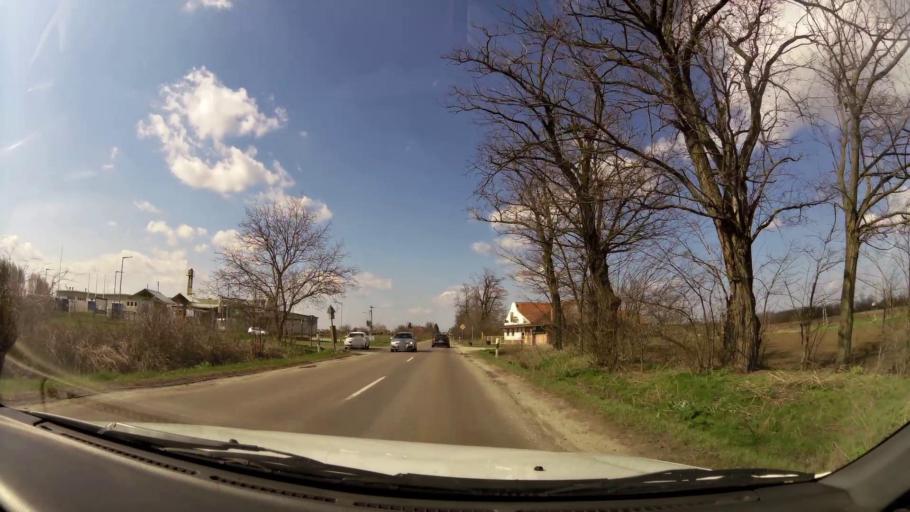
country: HU
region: Pest
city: Farmos
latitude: 47.3511
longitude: 19.8584
